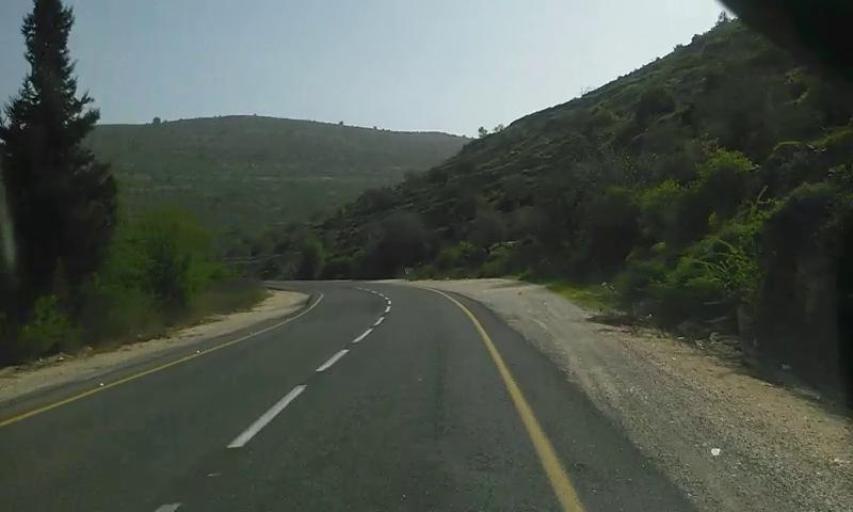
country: PS
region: West Bank
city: `Atarah
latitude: 31.9999
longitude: 35.2378
